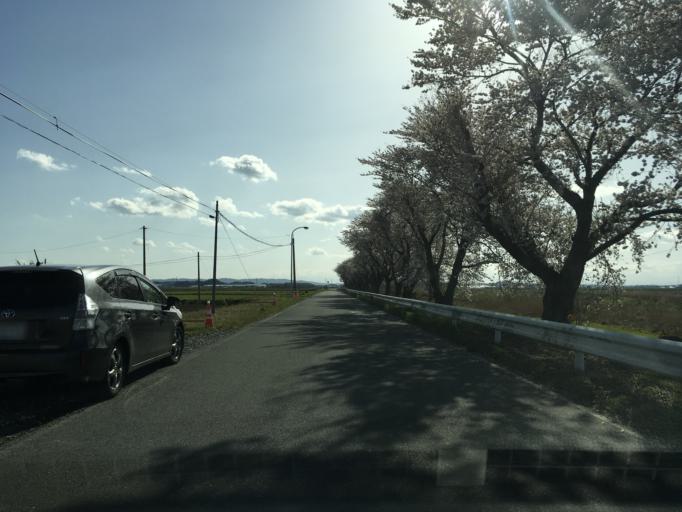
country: JP
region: Miyagi
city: Wakuya
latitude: 38.6657
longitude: 141.2512
